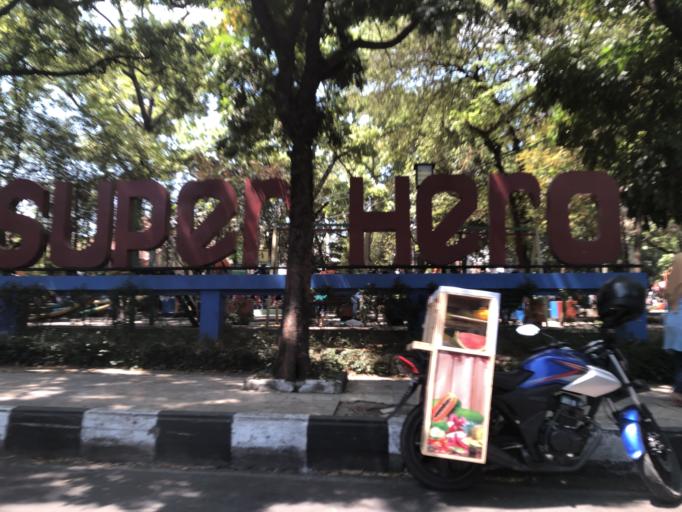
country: ID
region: West Java
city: Bandung
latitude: -6.9111
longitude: 107.6305
